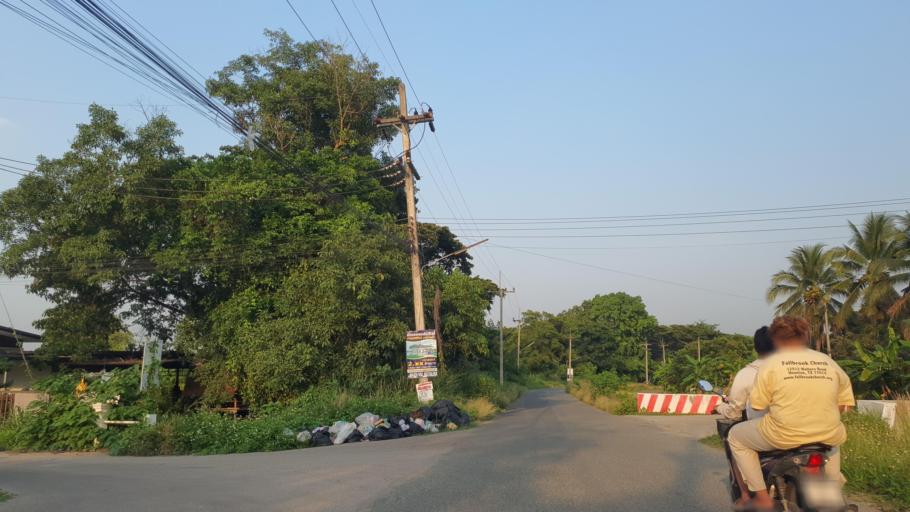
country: TH
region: Chiang Mai
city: Hang Dong
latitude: 18.6609
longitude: 98.9224
